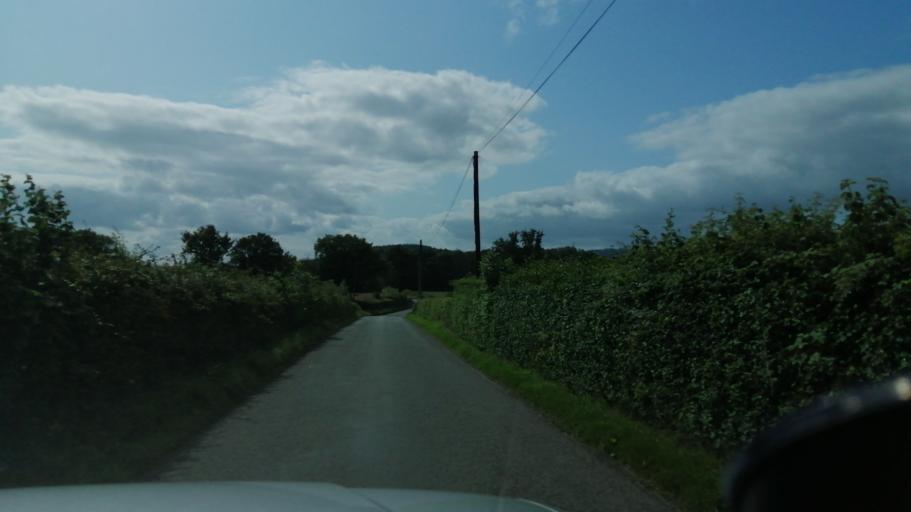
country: GB
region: England
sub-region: Herefordshire
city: Kinnersley
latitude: 52.1301
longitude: -2.9621
